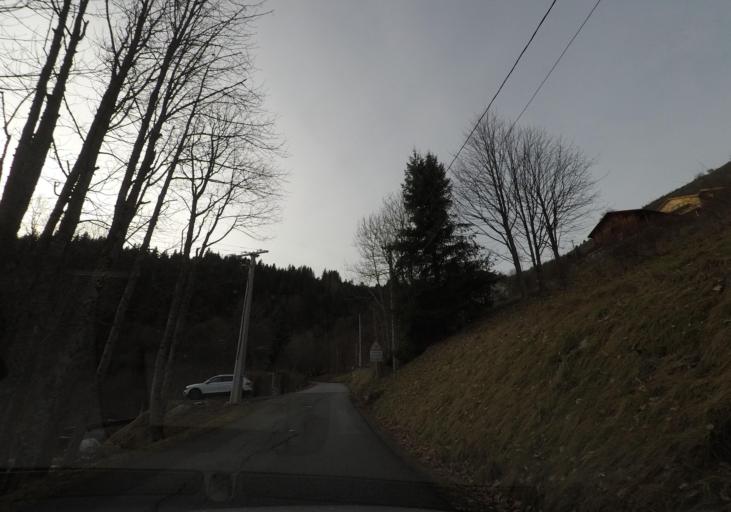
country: FR
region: Rhone-Alpes
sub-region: Departement de la Haute-Savoie
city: Ayse
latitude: 46.0427
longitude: 6.4373
